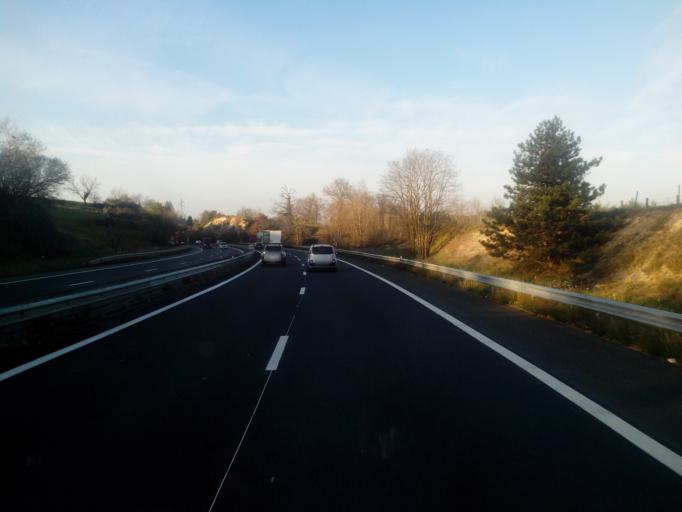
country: FR
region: Limousin
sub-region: Departement de la Correze
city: Brive-la-Gaillarde
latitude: 45.1201
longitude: 1.5010
